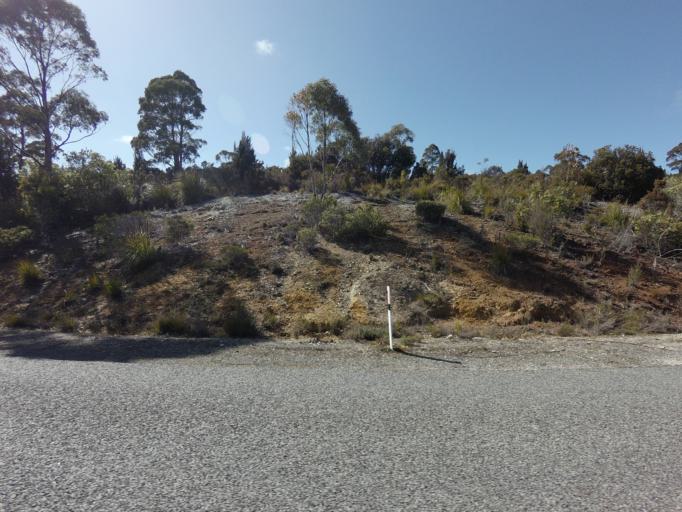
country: AU
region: Tasmania
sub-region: Derwent Valley
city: New Norfolk
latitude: -42.7608
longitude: 146.3968
